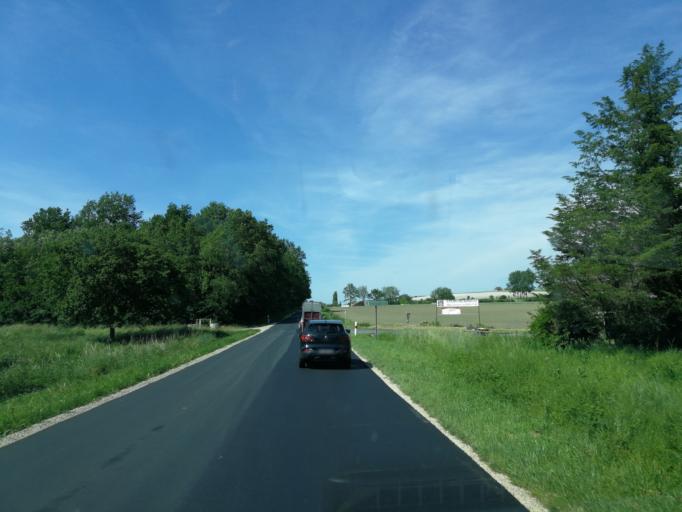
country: FR
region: Centre
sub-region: Departement d'Indre-et-Loire
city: Ligre
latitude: 47.1008
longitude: 0.1895
